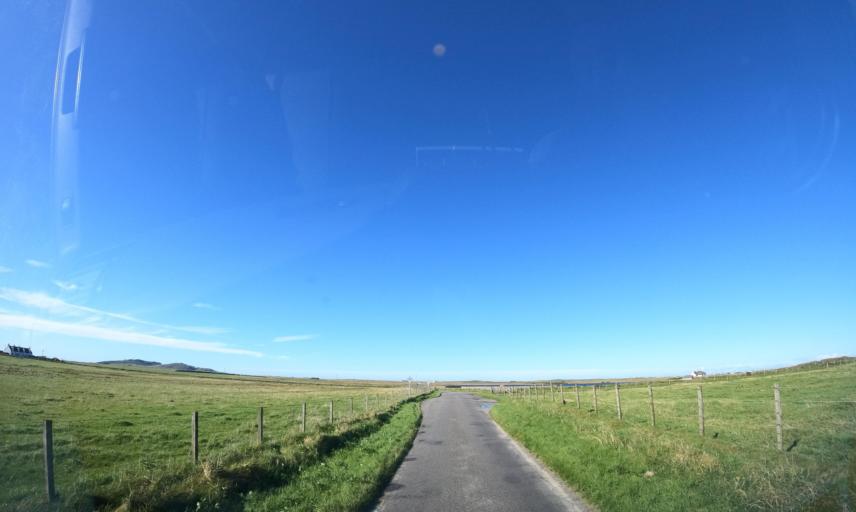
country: GB
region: Scotland
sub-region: Eilean Siar
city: Barra
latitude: 56.4832
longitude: -6.9012
